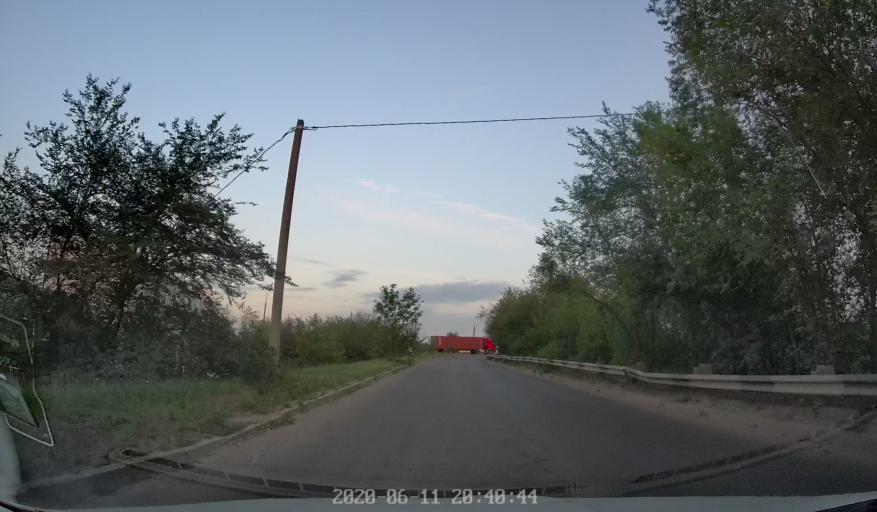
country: MD
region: Chisinau
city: Chisinau
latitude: 46.9845
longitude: 28.9034
